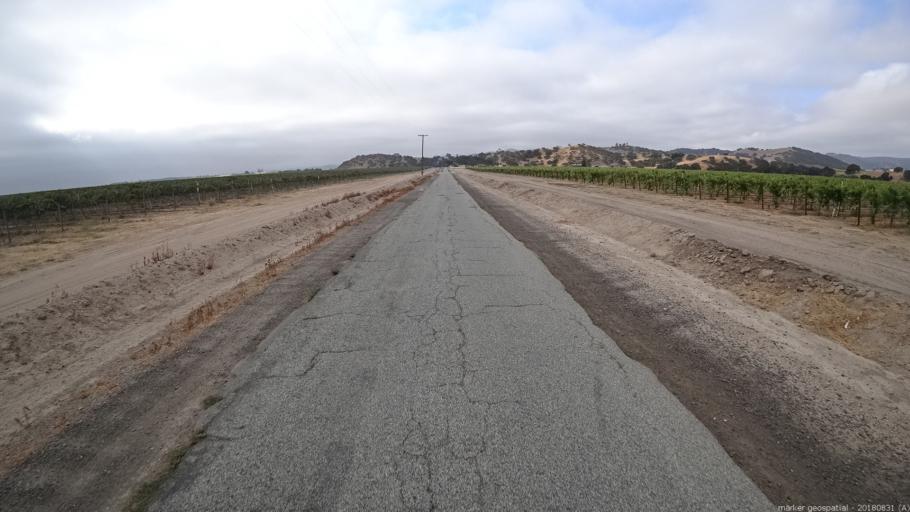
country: US
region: California
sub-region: Monterey County
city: King City
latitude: 36.1467
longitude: -121.1006
